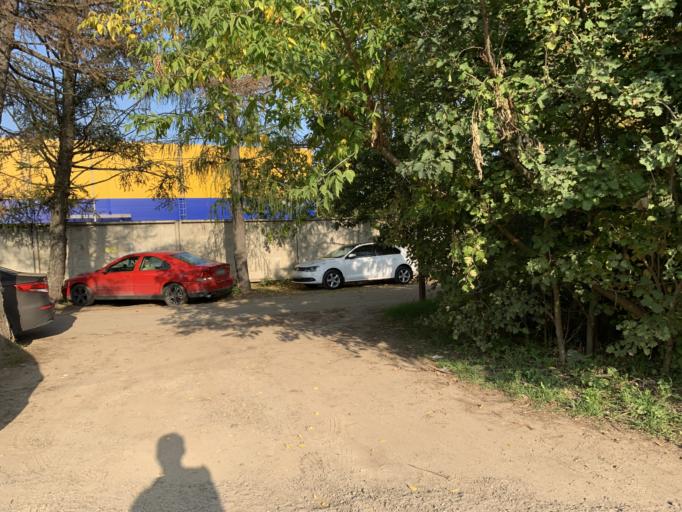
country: RU
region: Moskovskaya
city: Lesnyye Polyany
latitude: 55.9673
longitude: 37.8465
